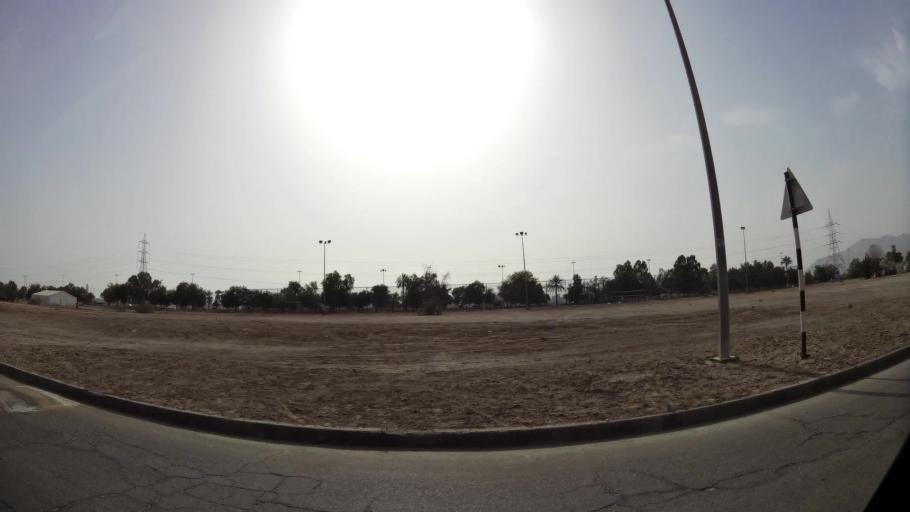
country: AE
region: Abu Dhabi
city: Al Ain
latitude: 24.1402
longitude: 55.7114
